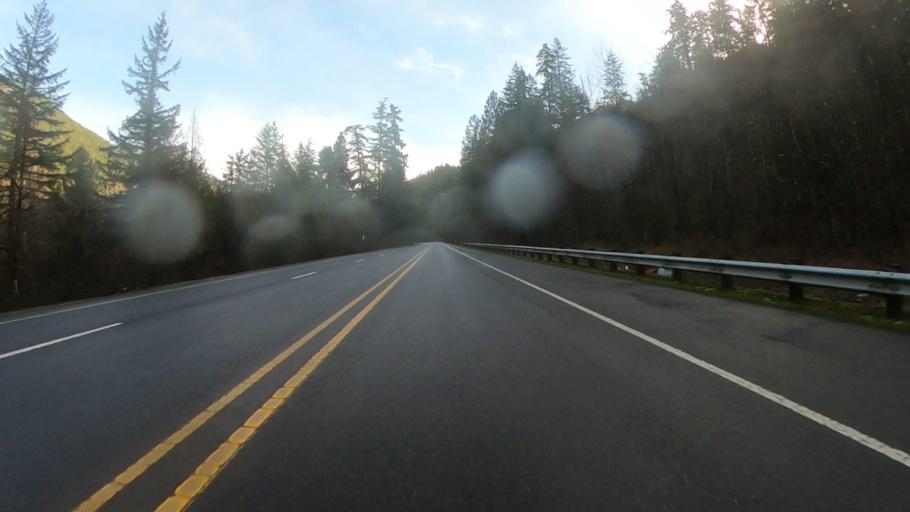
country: US
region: Oregon
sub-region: Lane County
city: Oakridge
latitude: 43.7292
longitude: -122.3794
